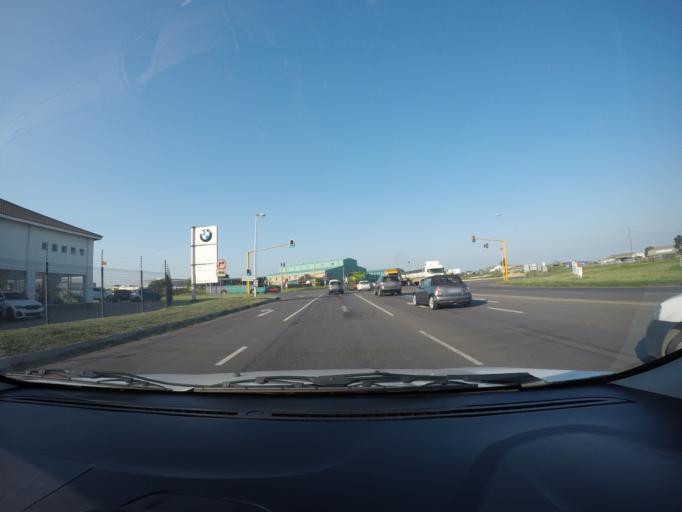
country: ZA
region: KwaZulu-Natal
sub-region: uThungulu District Municipality
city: Richards Bay
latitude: -28.7541
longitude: 32.0256
